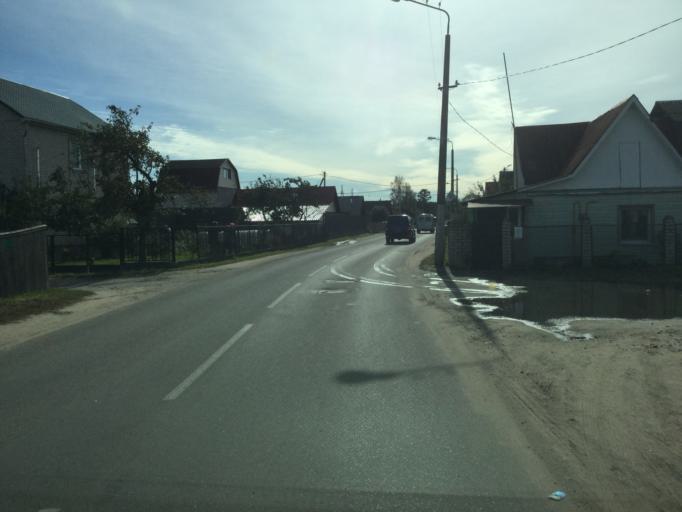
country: BY
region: Vitebsk
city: Horad Orsha
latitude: 54.5484
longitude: 30.4310
